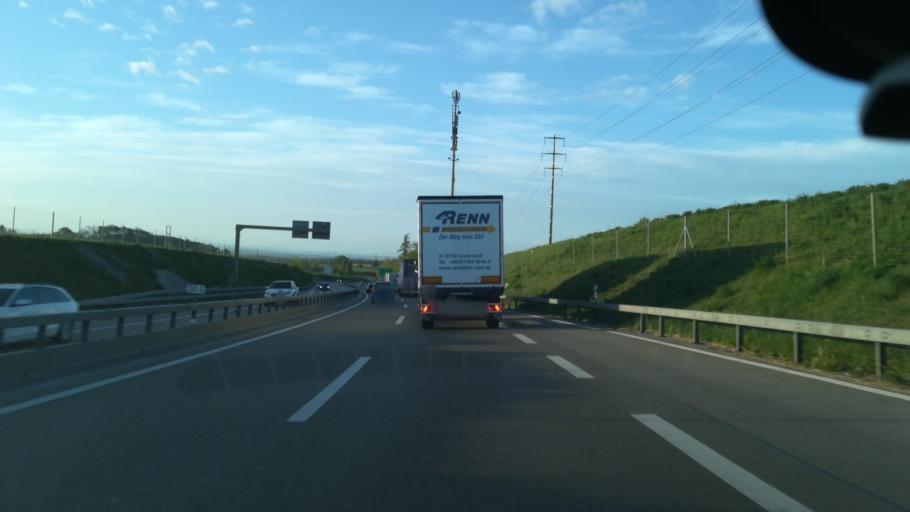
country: CH
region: Zurich
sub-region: Bezirk Andelfingen
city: Dachsen
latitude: 47.6703
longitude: 8.6227
